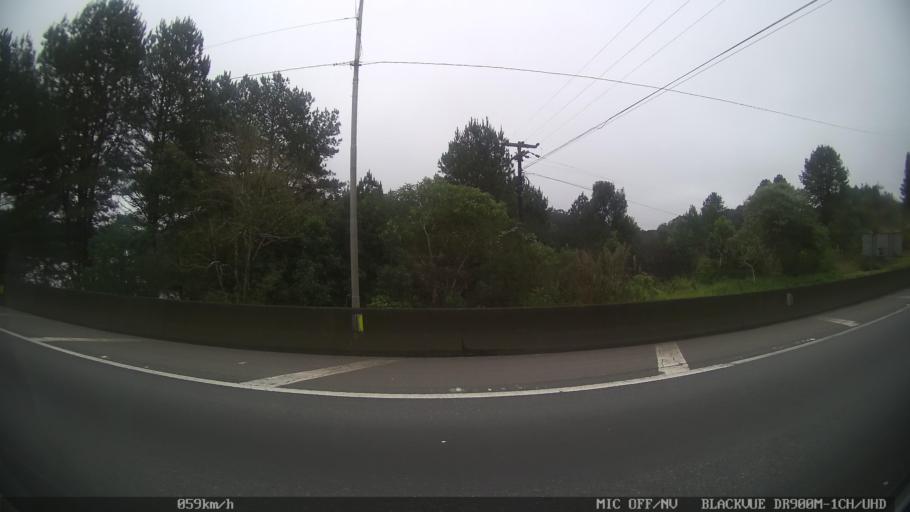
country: BR
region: Parana
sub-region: Sao Jose Dos Pinhais
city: Sao Jose dos Pinhais
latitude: -25.8426
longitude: -49.0550
